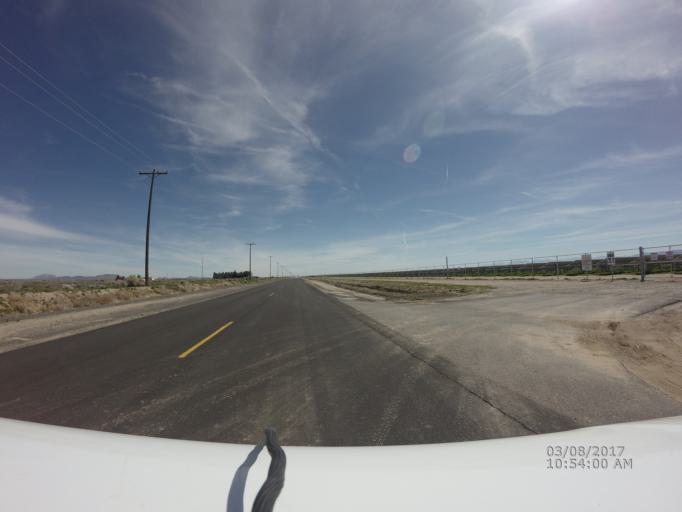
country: US
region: California
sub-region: Los Angeles County
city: Green Valley
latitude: 34.8192
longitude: -118.3865
